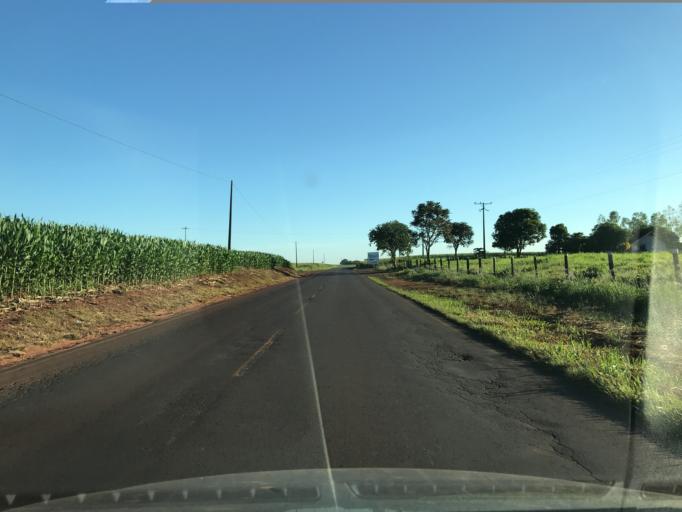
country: BR
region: Parana
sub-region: Palotina
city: Palotina
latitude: -24.1191
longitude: -53.8480
